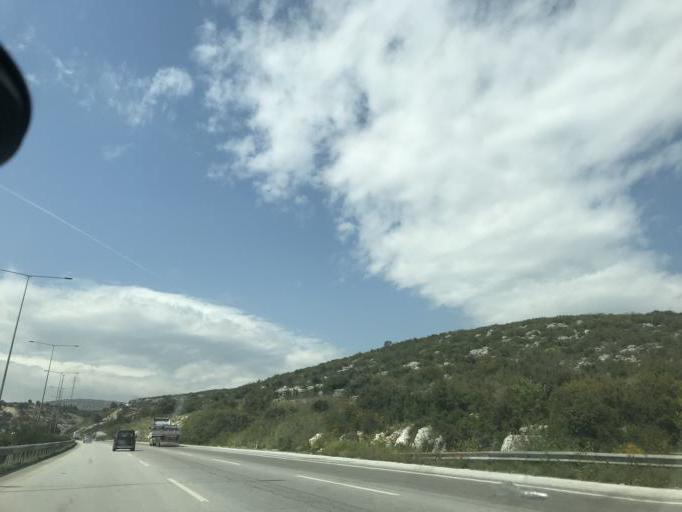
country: TR
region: Mersin
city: Tarsus
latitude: 37.1464
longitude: 34.8417
